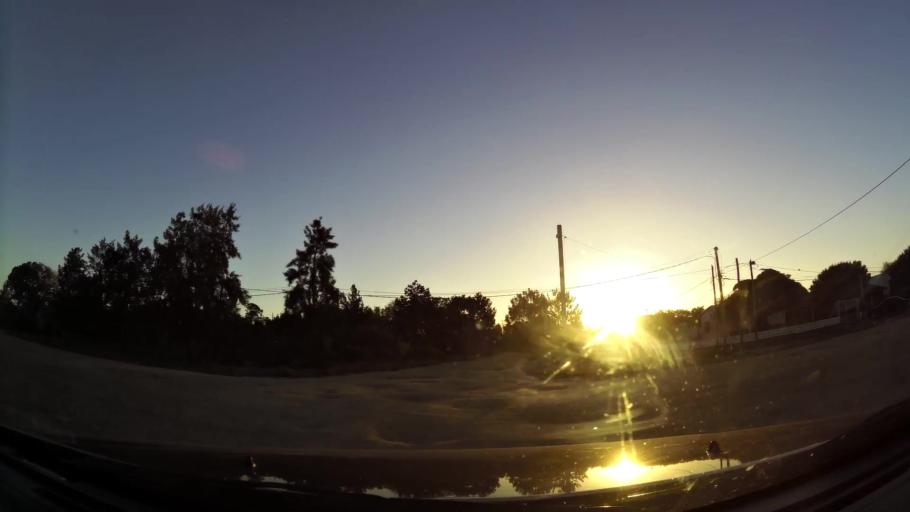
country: UY
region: Canelones
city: Barra de Carrasco
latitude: -34.8408
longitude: -55.9878
